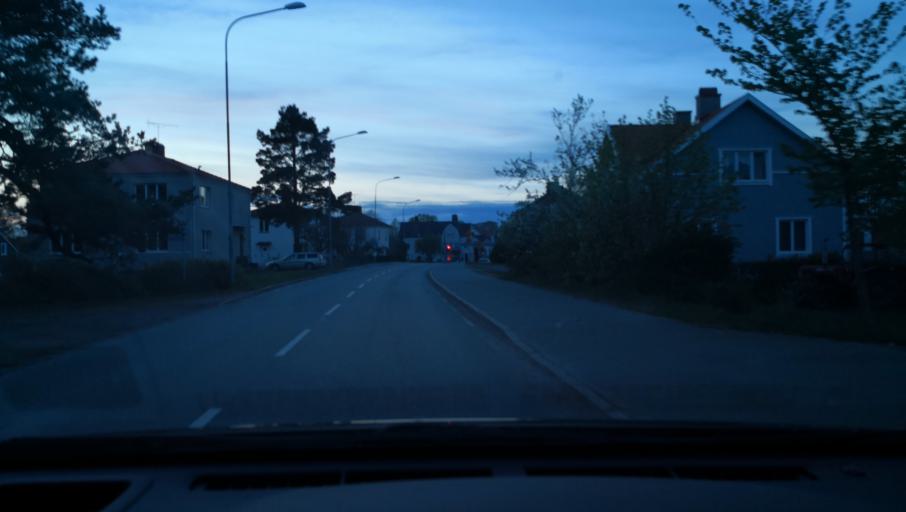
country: SE
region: OErebro
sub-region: Askersunds Kommun
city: Askersund
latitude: 59.0215
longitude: 14.8709
